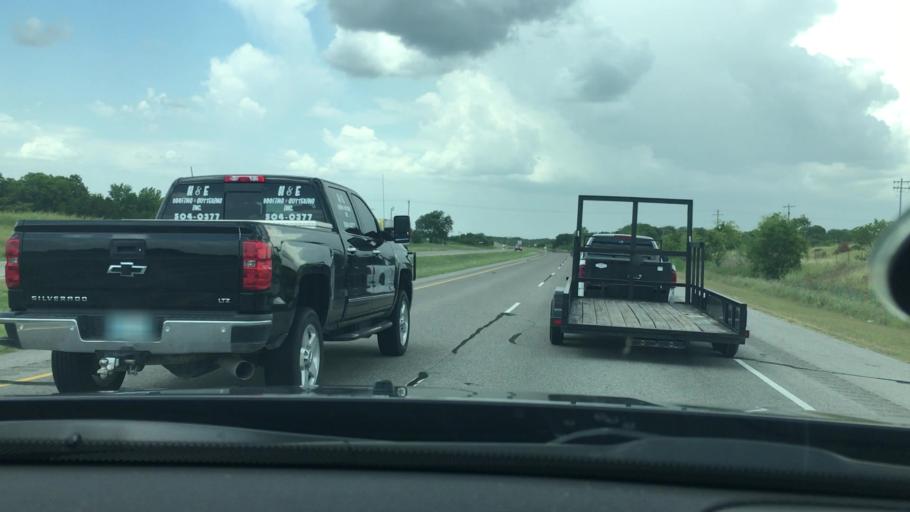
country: US
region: Oklahoma
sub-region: Carter County
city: Ardmore
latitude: 34.1382
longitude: -97.1224
